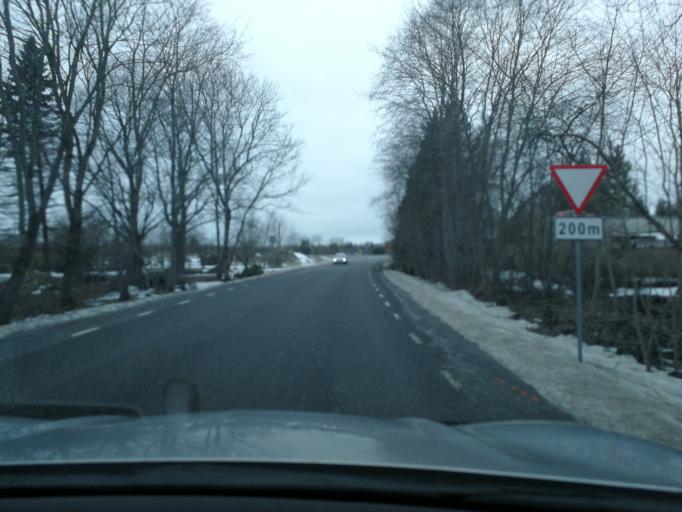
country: EE
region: Harju
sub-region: Saue linn
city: Saue
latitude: 59.3082
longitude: 24.5728
